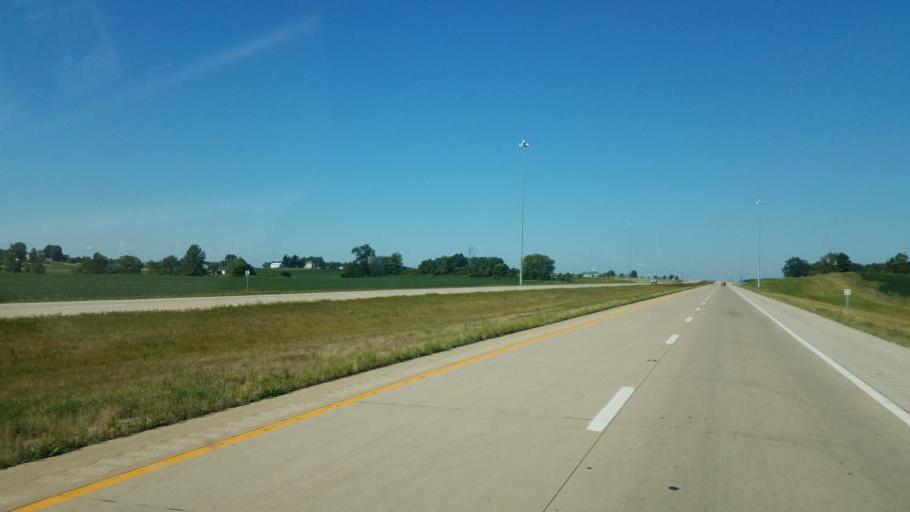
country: US
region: Ohio
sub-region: Wyandot County
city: Upper Sandusky
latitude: 40.8081
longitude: -83.1604
